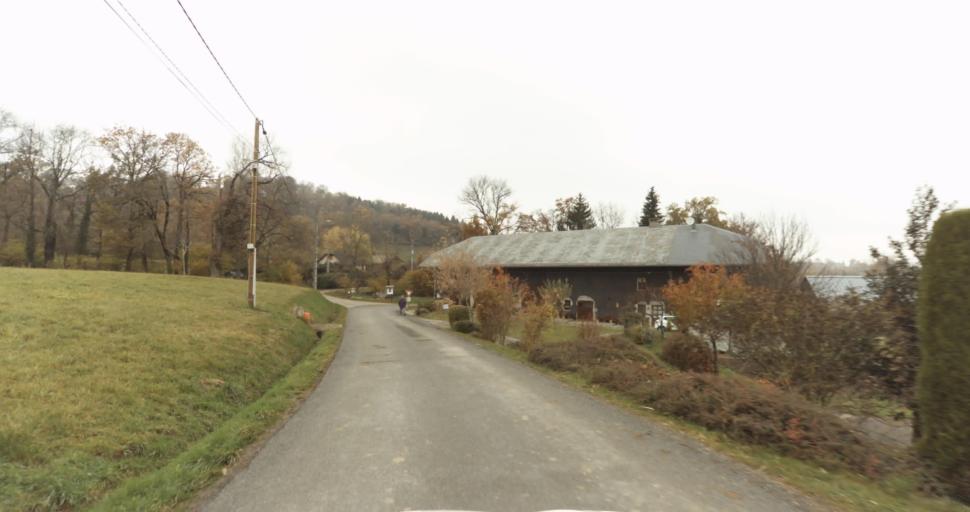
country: FR
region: Rhone-Alpes
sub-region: Departement de la Haute-Savoie
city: Cusy
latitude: 45.7846
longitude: 6.0139
